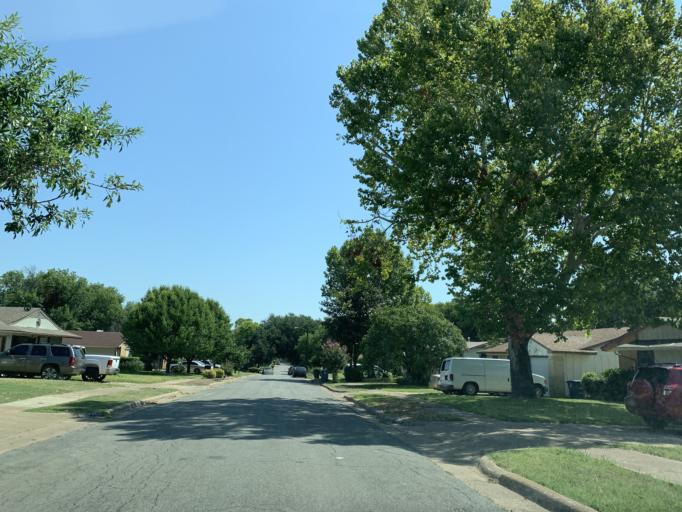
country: US
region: Texas
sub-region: Dallas County
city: Hutchins
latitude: 32.6731
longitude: -96.7532
